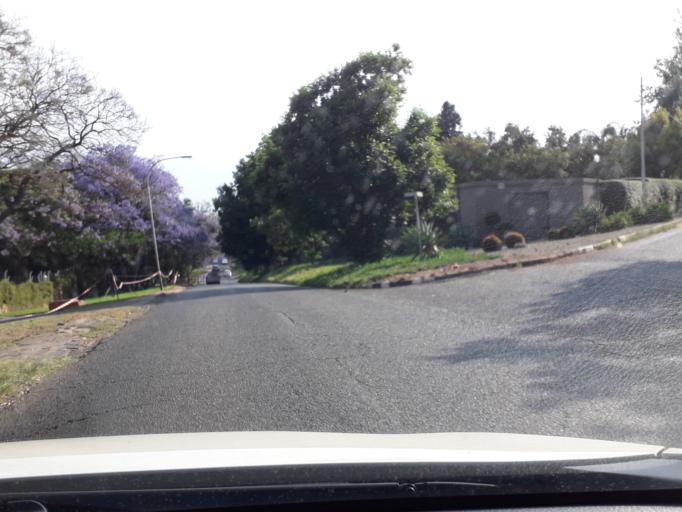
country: ZA
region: Gauteng
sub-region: City of Johannesburg Metropolitan Municipality
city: Roodepoort
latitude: -26.1442
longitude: 27.9602
